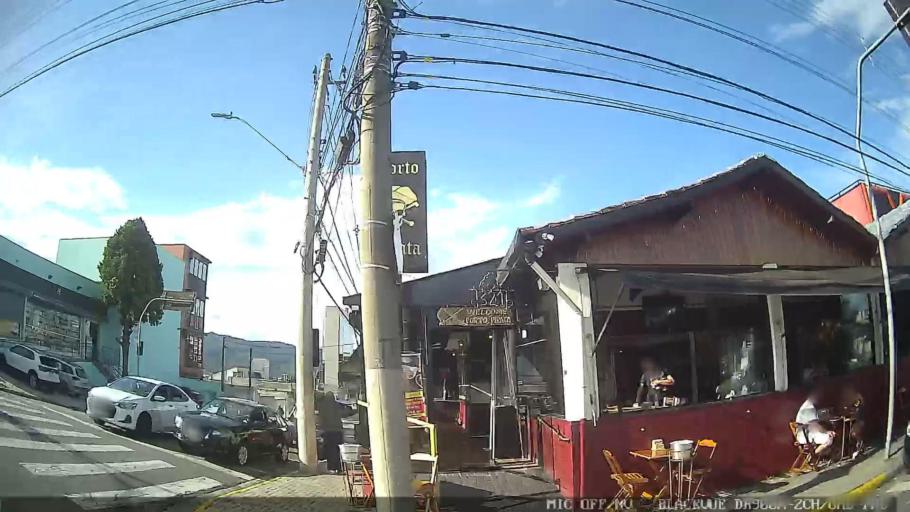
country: BR
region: Sao Paulo
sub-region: Mogi das Cruzes
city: Mogi das Cruzes
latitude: -23.5215
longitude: -46.1827
